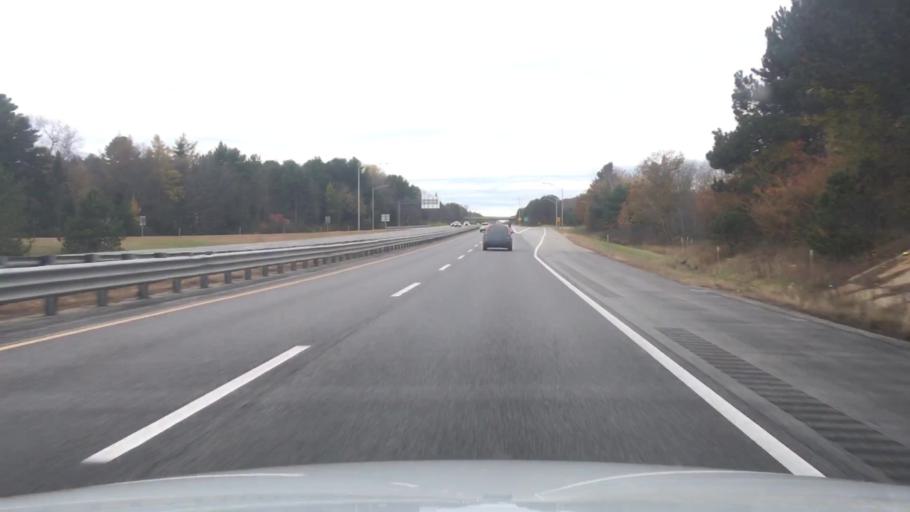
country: US
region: Maine
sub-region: Sagadahoc County
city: Topsham
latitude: 43.9177
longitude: -70.0207
